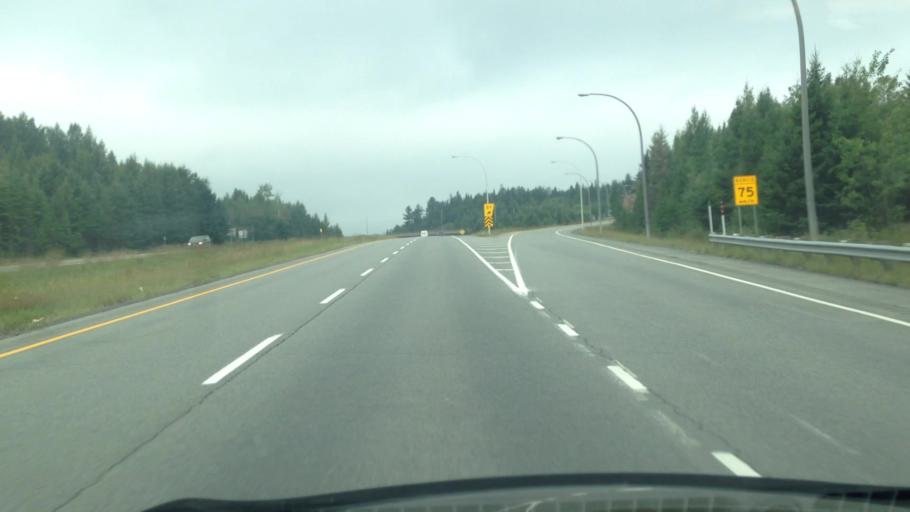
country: CA
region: Quebec
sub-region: Laurentides
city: Sainte-Agathe-des-Monts
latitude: 46.0623
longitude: -74.2832
